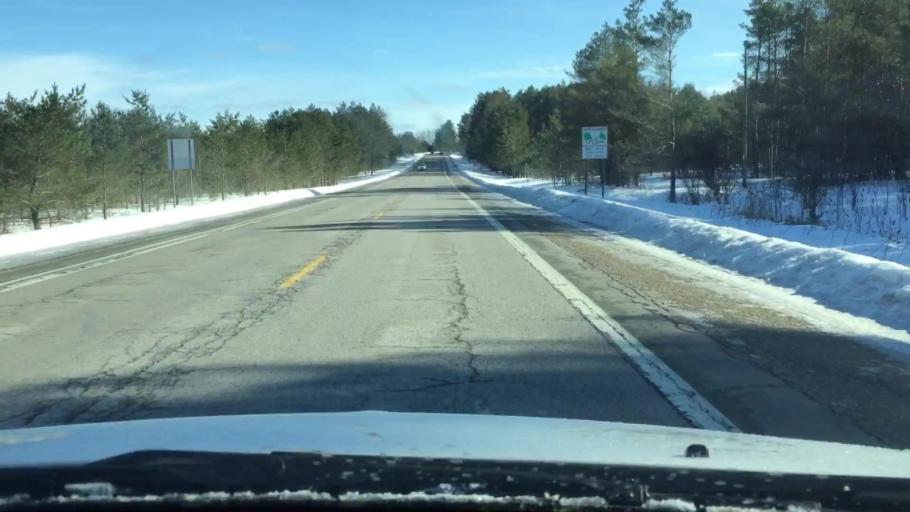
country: US
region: Michigan
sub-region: Charlevoix County
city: East Jordan
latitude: 45.0963
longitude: -85.1044
